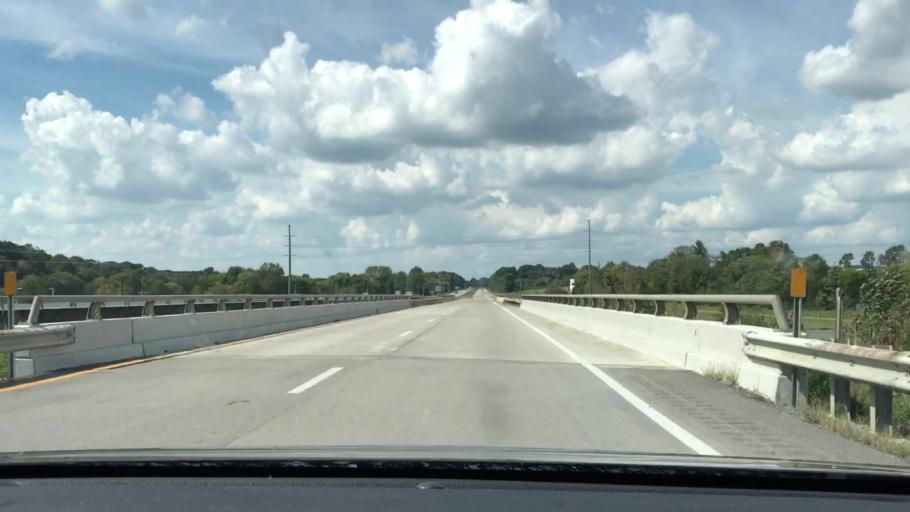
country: US
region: Kentucky
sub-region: Barren County
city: Glasgow
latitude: 36.9774
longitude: -85.9333
